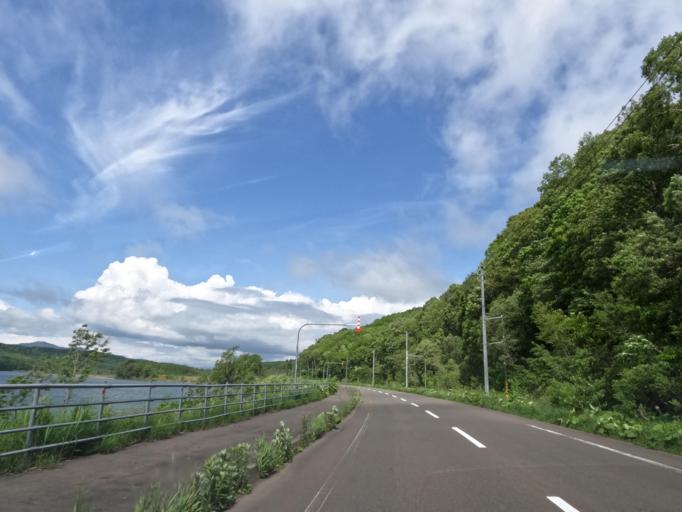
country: JP
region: Hokkaido
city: Tobetsu
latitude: 43.3629
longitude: 141.5709
